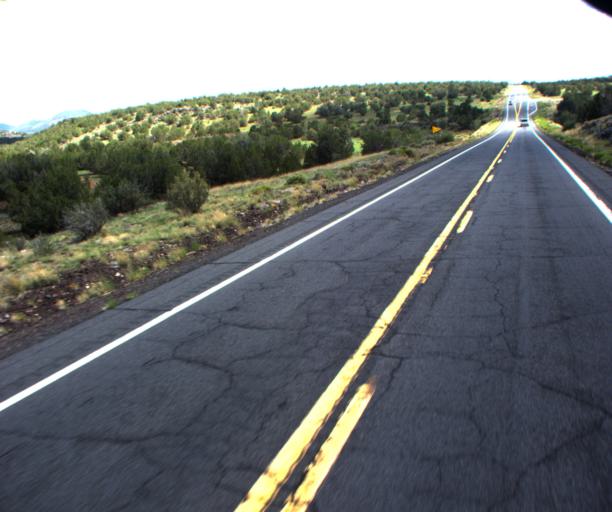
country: US
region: Arizona
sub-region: Coconino County
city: Williams
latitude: 35.4859
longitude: -112.1753
